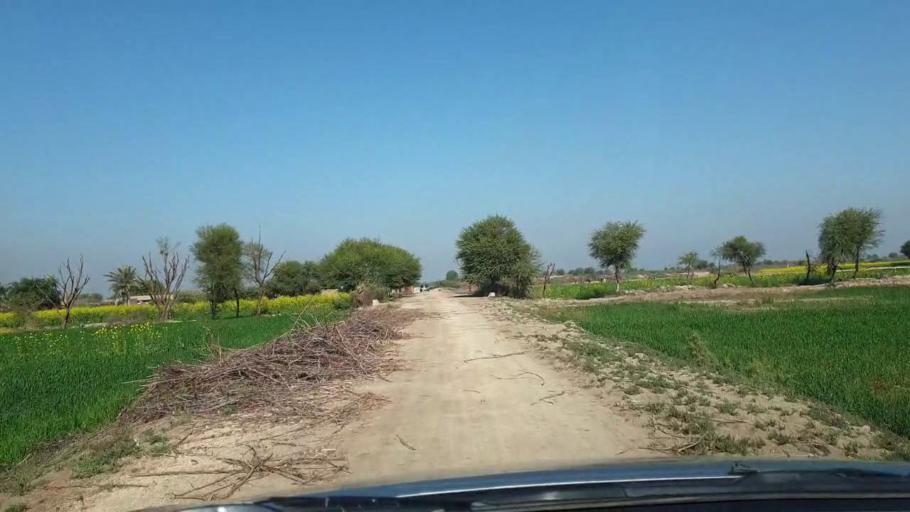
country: PK
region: Sindh
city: Jhol
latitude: 25.8830
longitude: 68.9184
